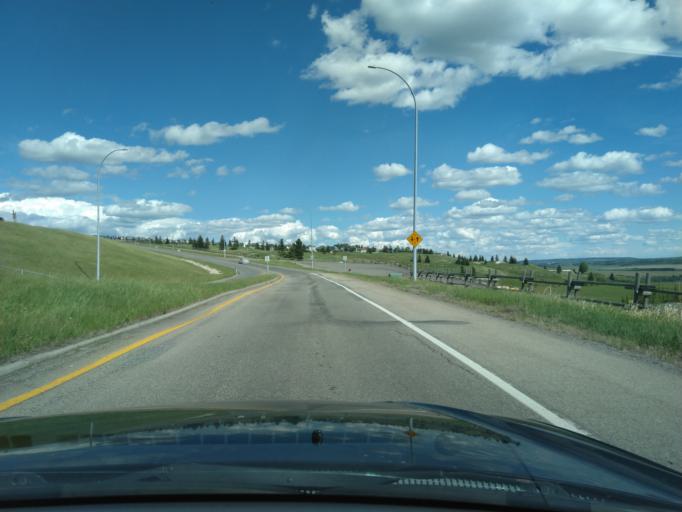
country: CA
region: Alberta
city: Cochrane
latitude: 51.1909
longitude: -114.4518
